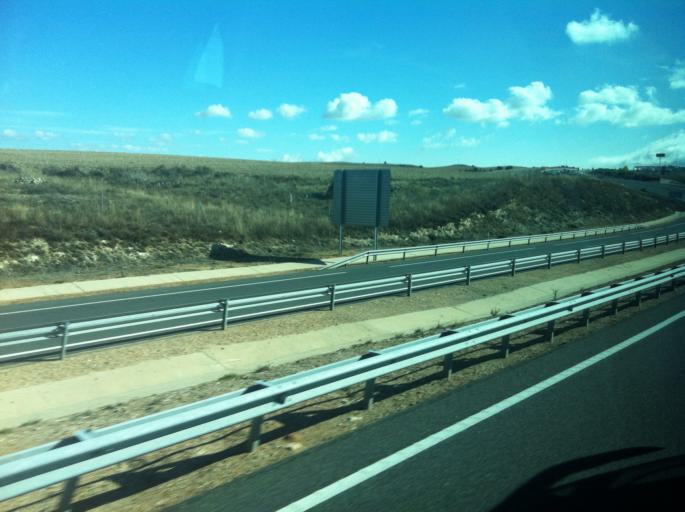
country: ES
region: Castille and Leon
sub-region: Provincia de Burgos
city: Fontioso
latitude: 41.9220
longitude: -3.7563
